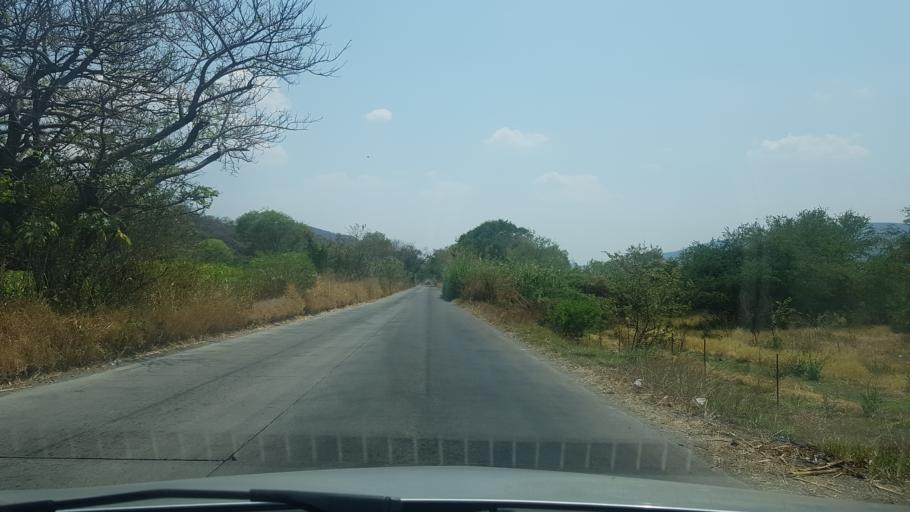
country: MX
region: Morelos
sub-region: Jiutepec
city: Independencia
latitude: 18.7942
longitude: -99.1031
